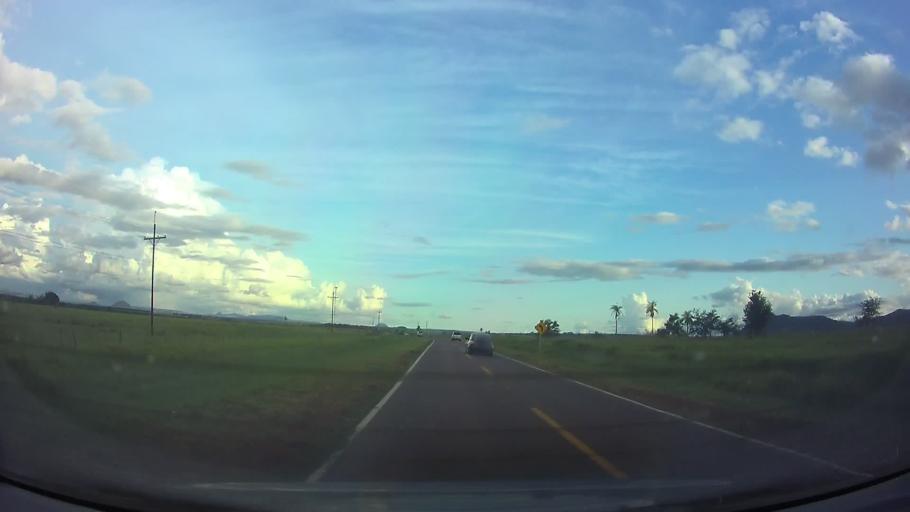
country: PY
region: Paraguari
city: Carapegua
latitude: -25.8250
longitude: -57.1646
